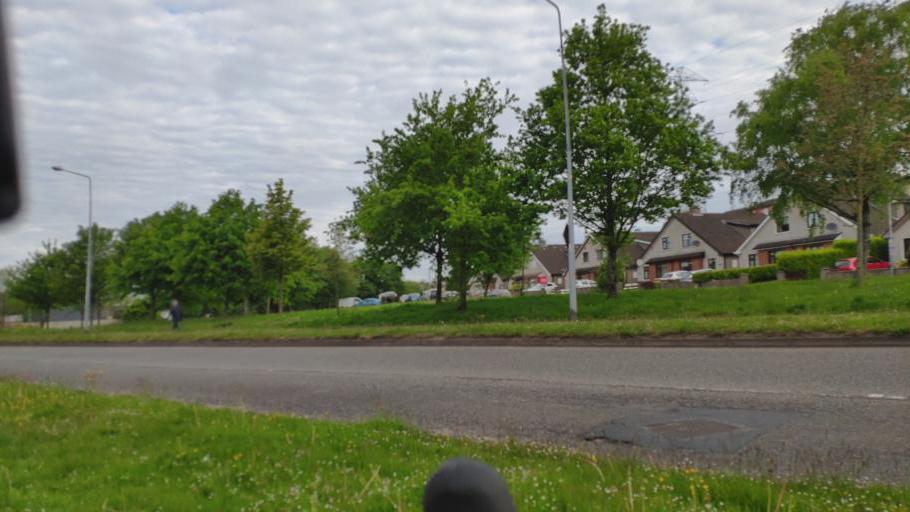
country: IE
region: Munster
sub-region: County Cork
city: Cork
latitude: 51.9157
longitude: -8.4524
